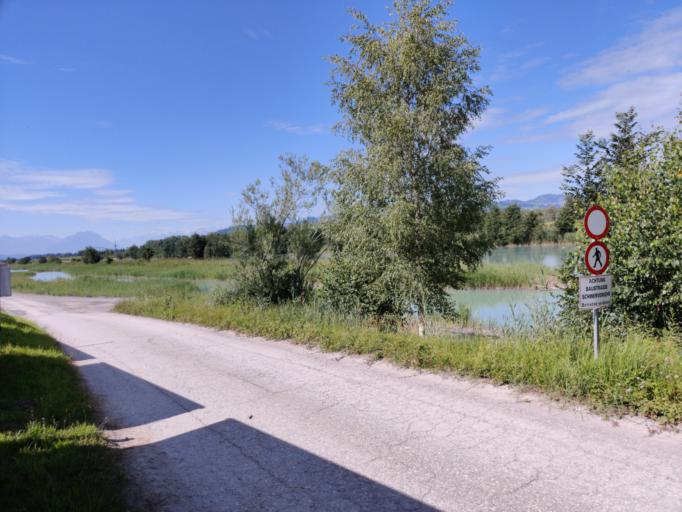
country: AT
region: Vorarlberg
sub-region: Politischer Bezirk Bregenz
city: Hard
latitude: 47.4977
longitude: 9.6720
